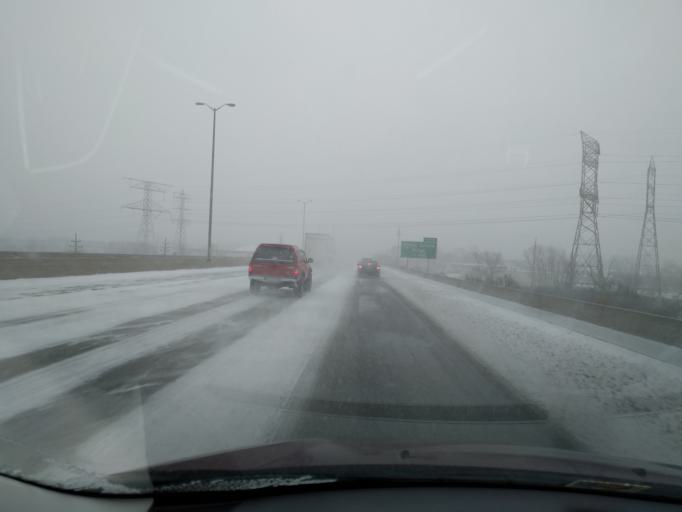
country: US
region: Wisconsin
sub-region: Waukesha County
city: Butler
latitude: 43.1283
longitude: -88.0231
